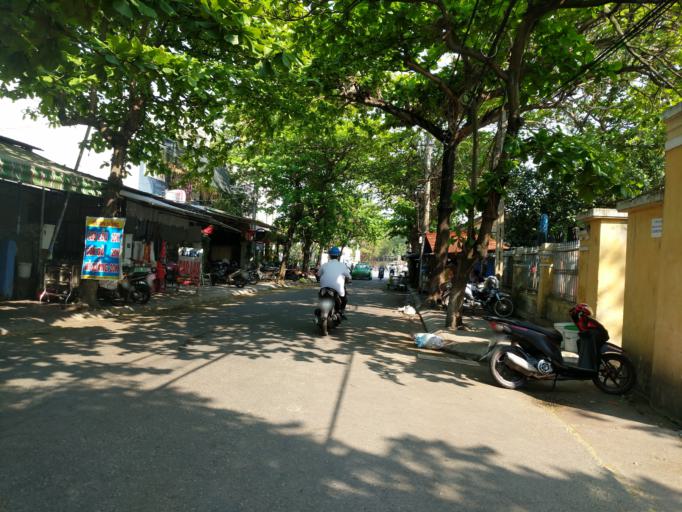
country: VN
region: Quang Nam
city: Hoi An
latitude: 15.8815
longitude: 108.3286
